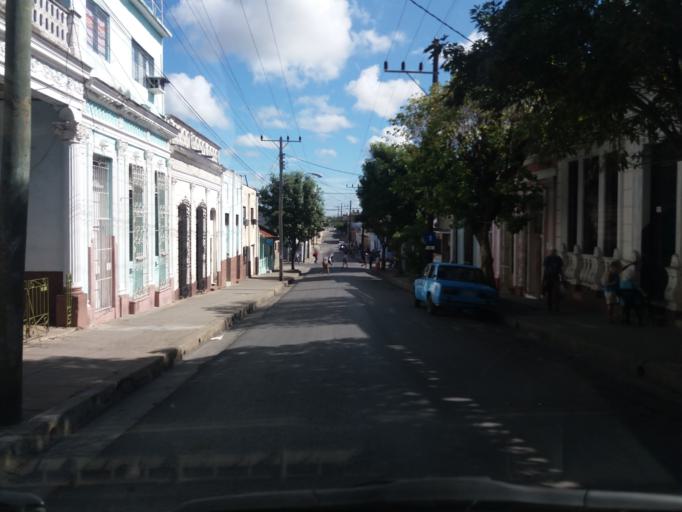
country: CU
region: Cienfuegos
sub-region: Municipio de Cienfuegos
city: Cienfuegos
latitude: 22.1477
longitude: -80.4471
